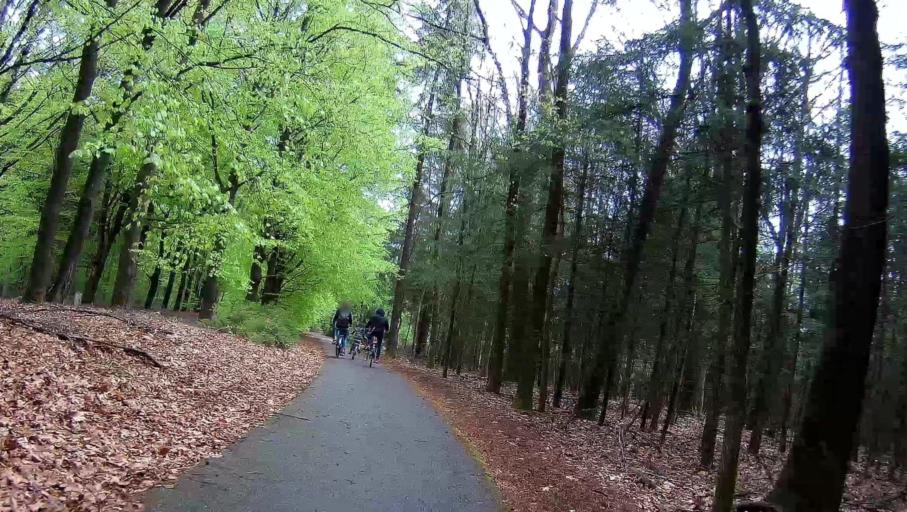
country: NL
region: Drenthe
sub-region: Gemeente Borger-Odoorn
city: Borger
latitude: 52.9474
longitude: 6.7238
